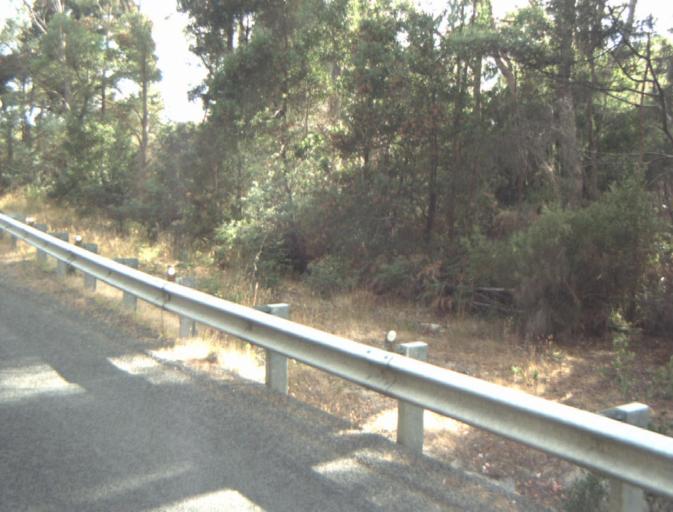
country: AU
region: Tasmania
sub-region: Dorset
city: Bridport
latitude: -41.1174
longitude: 147.2046
